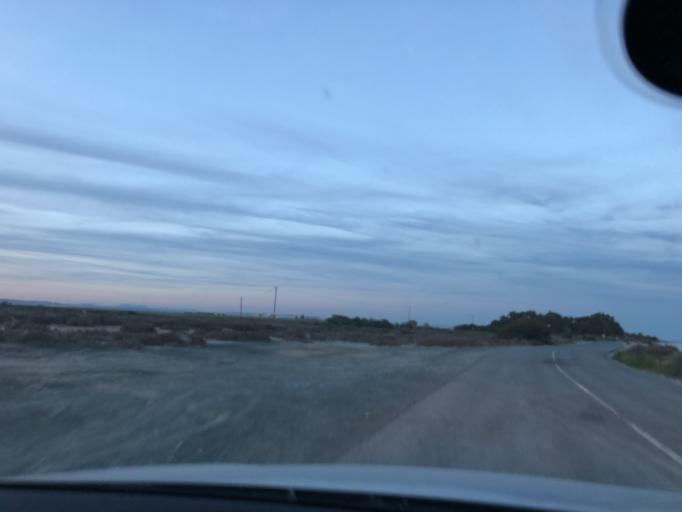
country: CY
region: Larnaka
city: Meneou
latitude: 34.8560
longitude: 33.6292
